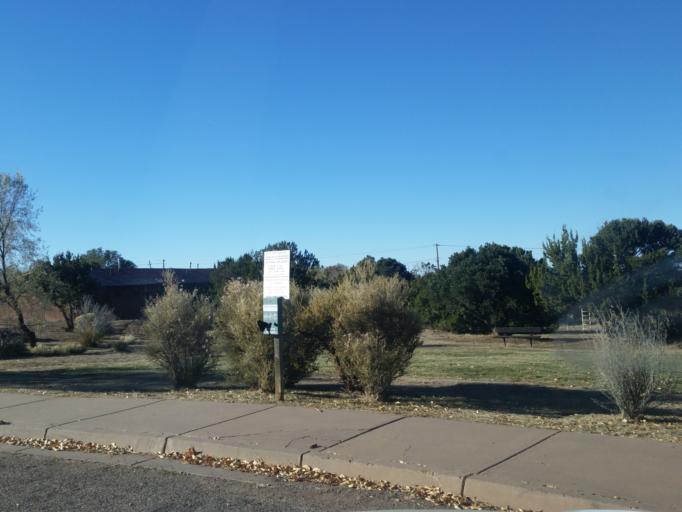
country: US
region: New Mexico
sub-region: Santa Fe County
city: Santa Fe
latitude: 35.6489
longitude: -105.9325
